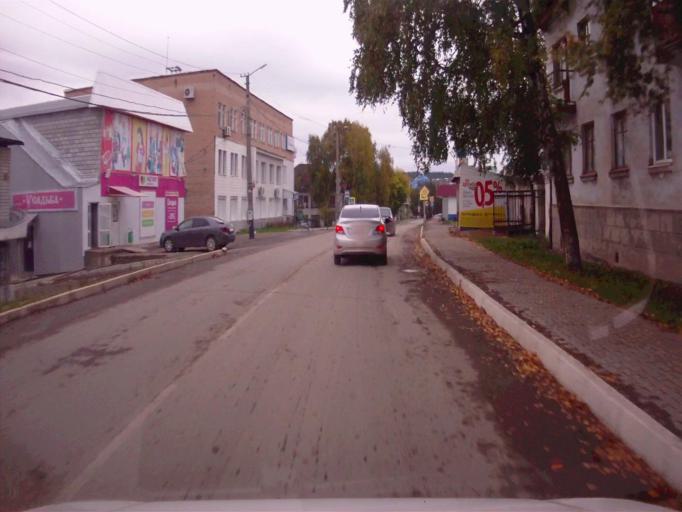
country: RU
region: Chelyabinsk
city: Nyazepetrovsk
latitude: 56.0535
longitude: 59.6015
